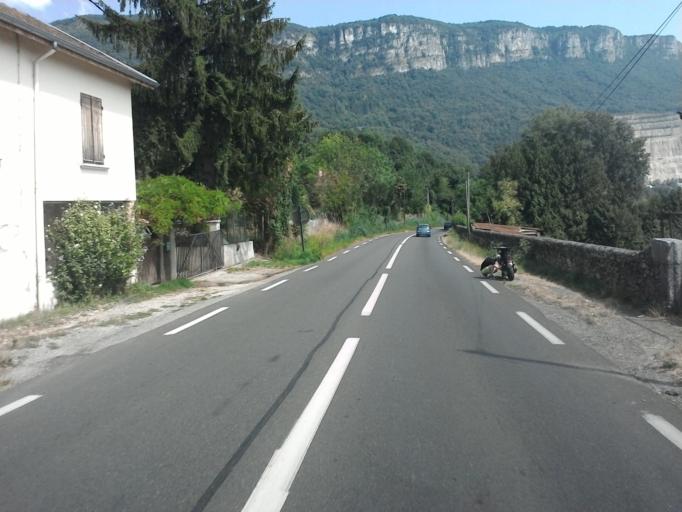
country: FR
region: Rhone-Alpes
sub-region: Departement de l'Isere
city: La Buisse
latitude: 45.3400
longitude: 5.6146
